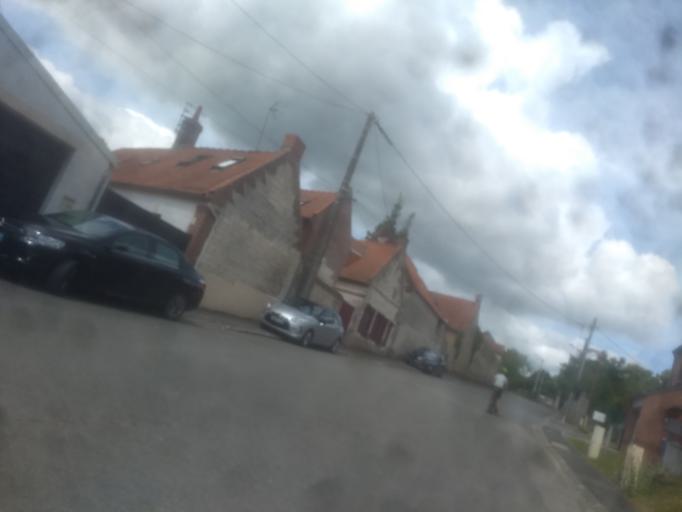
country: FR
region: Nord-Pas-de-Calais
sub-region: Departement du Pas-de-Calais
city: Maroeuil
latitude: 50.3247
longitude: 2.6999
